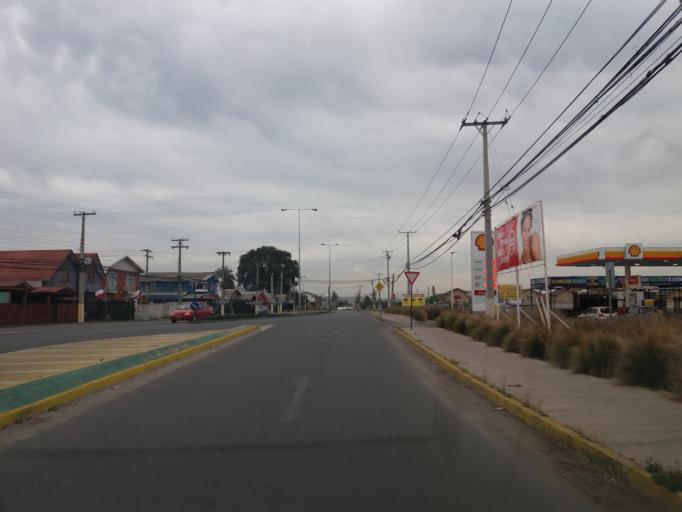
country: CL
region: Valparaiso
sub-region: Provincia de Quillota
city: Quillota
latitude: -32.8967
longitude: -71.2650
